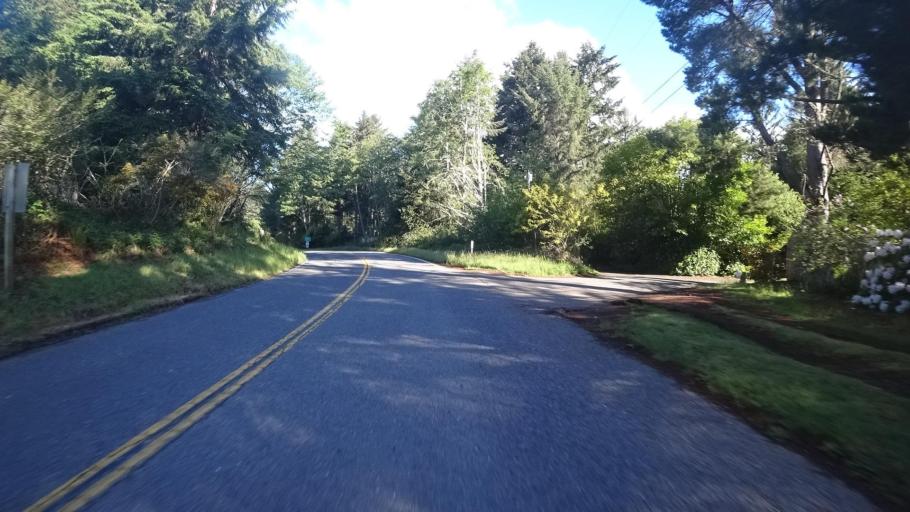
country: US
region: California
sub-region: Humboldt County
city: Westhaven-Moonstone
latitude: 41.0378
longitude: -124.1118
